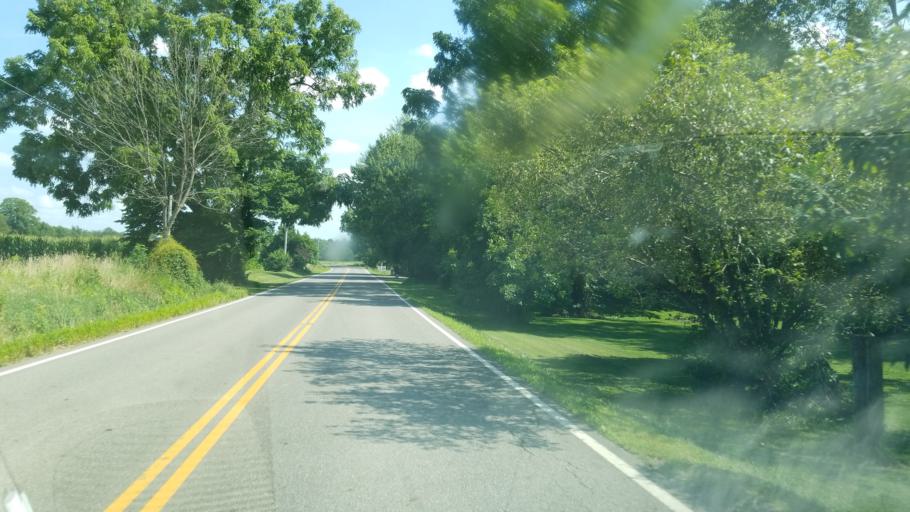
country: US
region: Ohio
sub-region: Huron County
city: Greenwich
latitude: 40.9330
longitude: -82.5397
